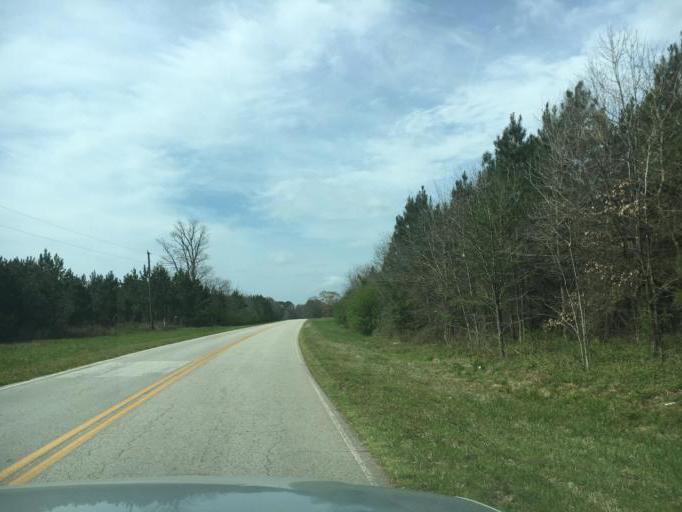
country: US
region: Georgia
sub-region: Franklin County
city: Lavonia
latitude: 34.4185
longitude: -83.0678
